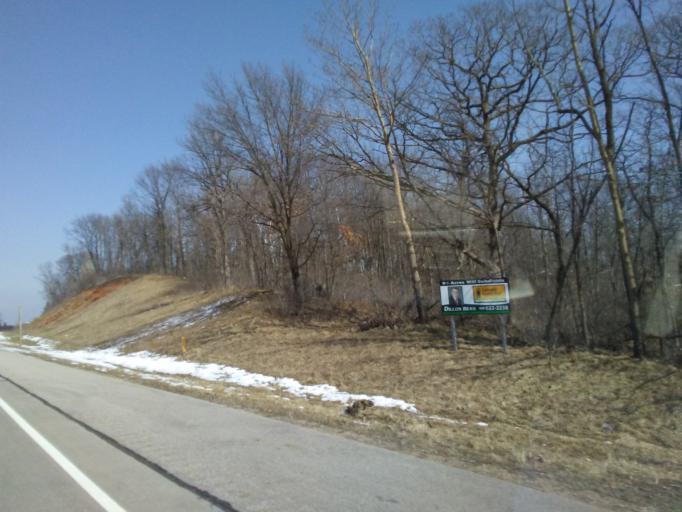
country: US
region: Wisconsin
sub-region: Vernon County
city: Viroqua
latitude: 43.6049
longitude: -90.8888
